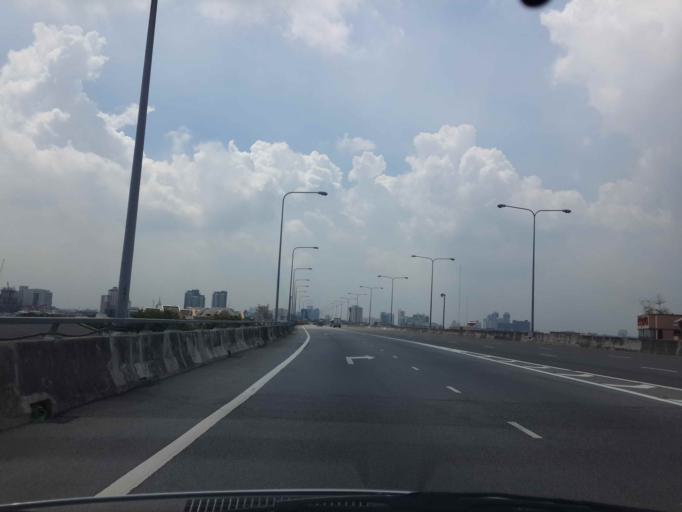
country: TH
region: Bangkok
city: Phra Khanong
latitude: 13.6964
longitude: 100.5946
